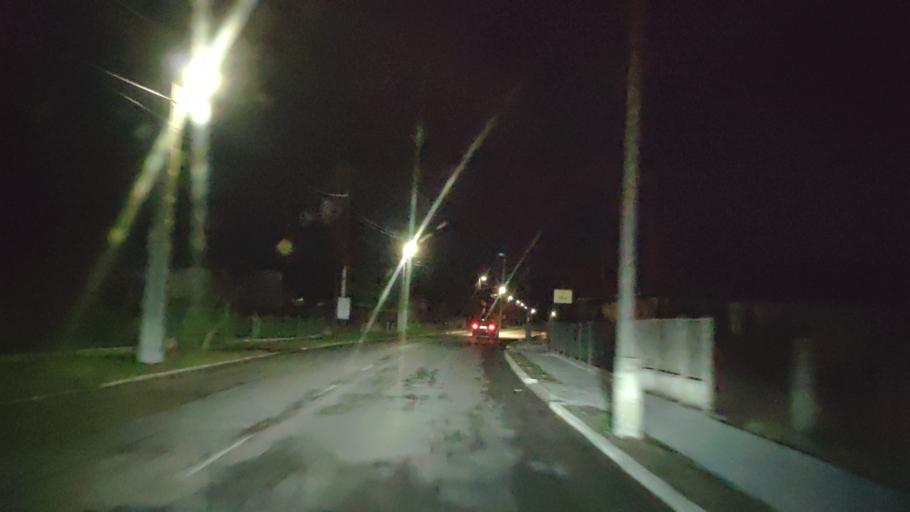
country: HU
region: Borsod-Abauj-Zemplen
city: Satoraljaujhely
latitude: 48.4645
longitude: 21.5951
